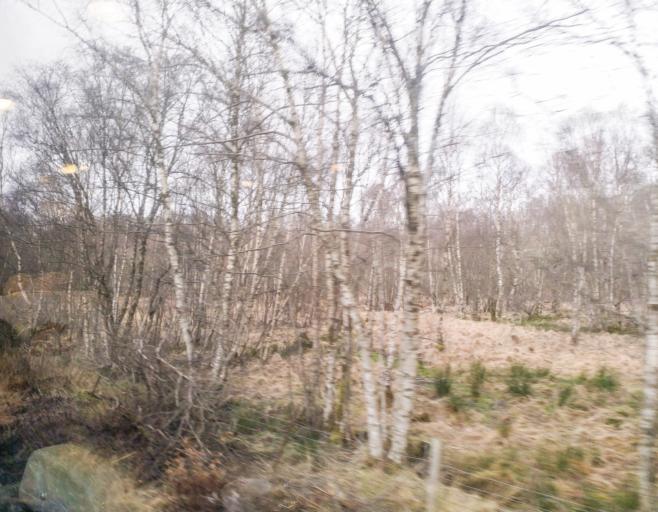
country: GB
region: Scotland
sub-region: Highland
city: Spean Bridge
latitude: 56.8875
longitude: -4.8301
